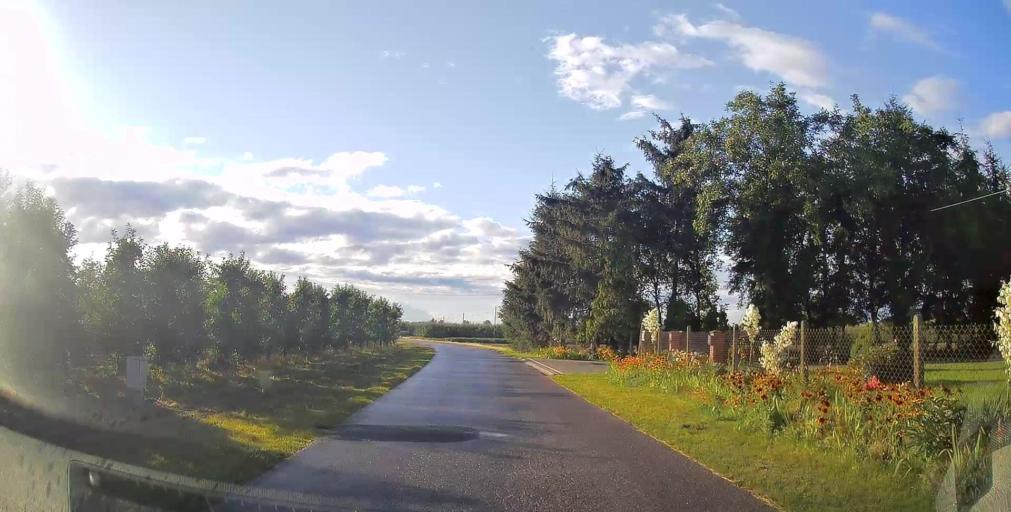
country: PL
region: Masovian Voivodeship
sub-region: Powiat grojecki
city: Goszczyn
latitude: 51.7518
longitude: 20.8846
